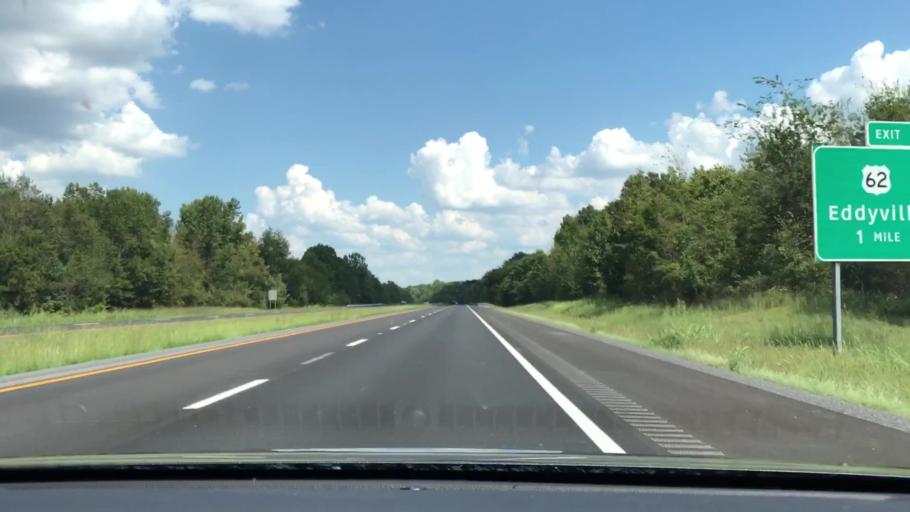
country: US
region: Kentucky
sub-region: Lyon County
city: Eddyville
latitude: 37.0924
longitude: -88.0506
